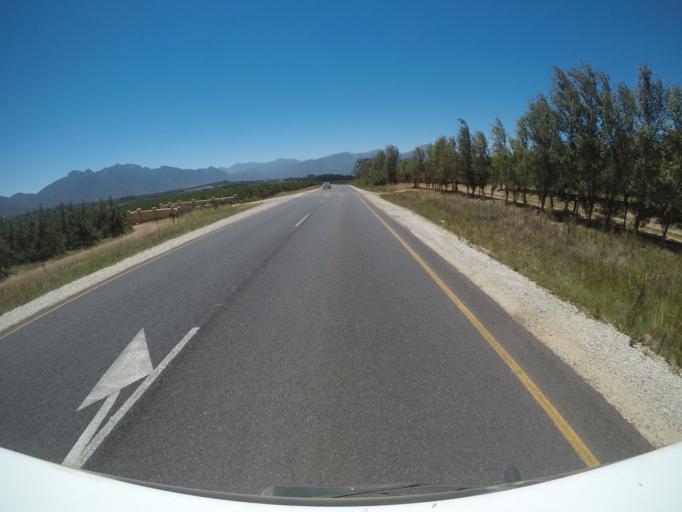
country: ZA
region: Western Cape
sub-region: Overberg District Municipality
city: Grabouw
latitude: -34.0617
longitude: 19.1352
